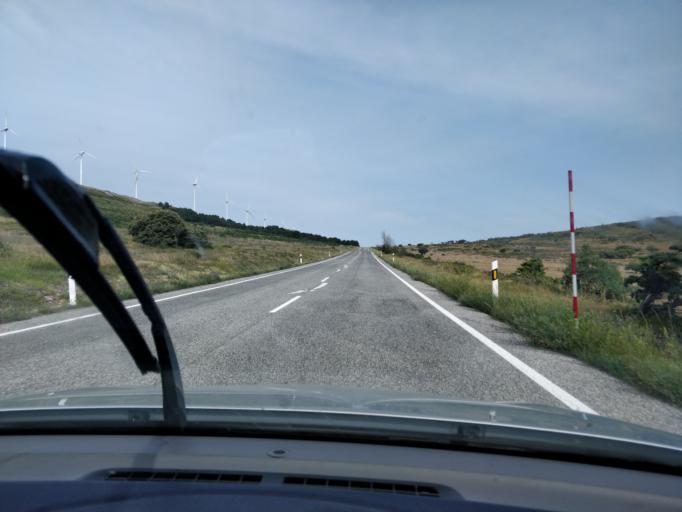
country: ES
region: Castille and Leon
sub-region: Provincia de Burgos
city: Medina de Pomar
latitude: 42.9270
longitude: -3.6388
